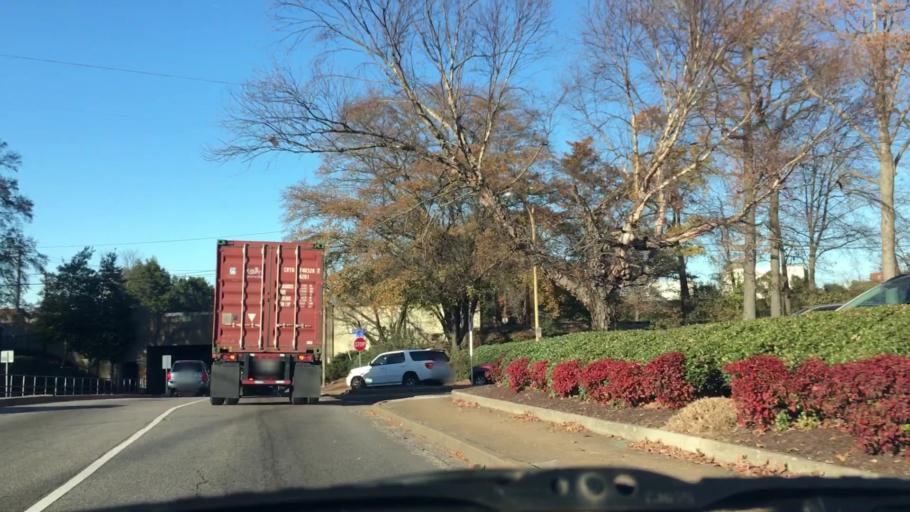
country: US
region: Virginia
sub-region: City of Norfolk
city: Norfolk
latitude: 36.8729
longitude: -76.3015
